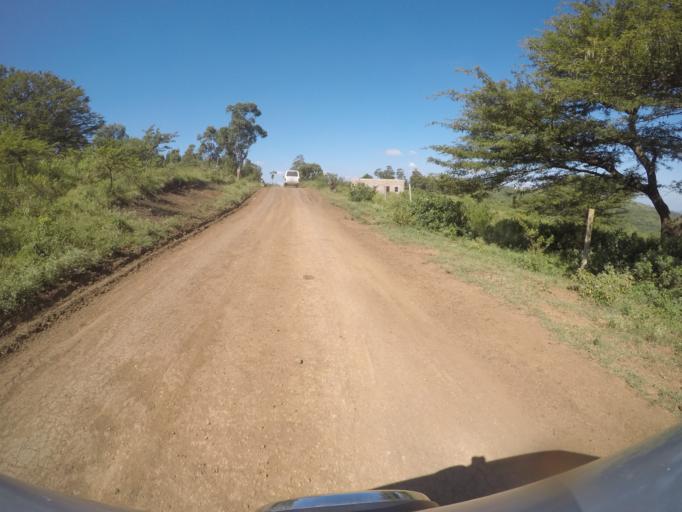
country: ZA
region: KwaZulu-Natal
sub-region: uThungulu District Municipality
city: Empangeni
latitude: -28.5648
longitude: 31.6992
